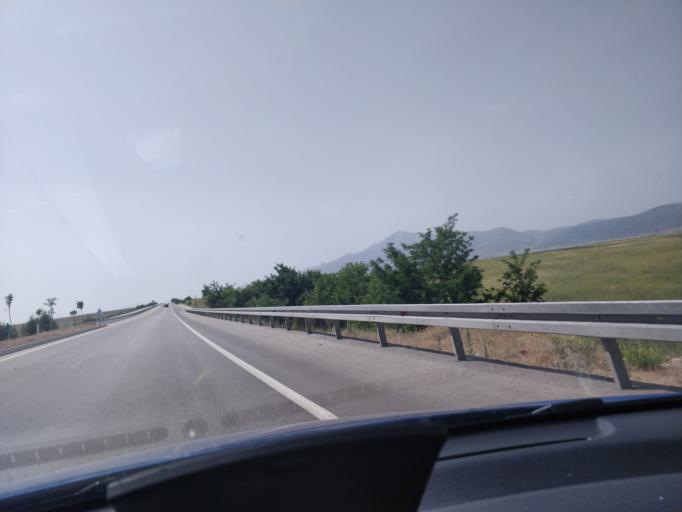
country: TR
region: Konya
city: Guneysinir
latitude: 37.3457
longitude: 32.8134
